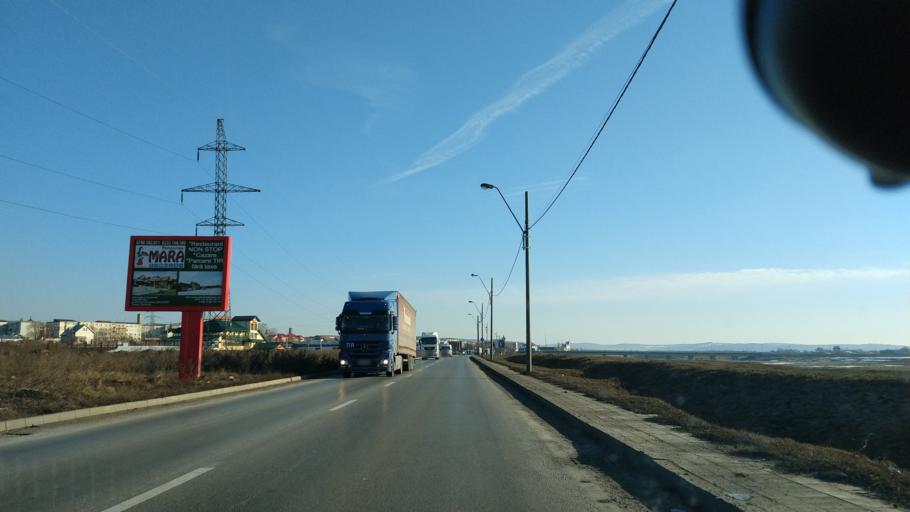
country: RO
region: Neamt
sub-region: Municipiul Roman
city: Roman
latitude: 46.9214
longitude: 26.9142
